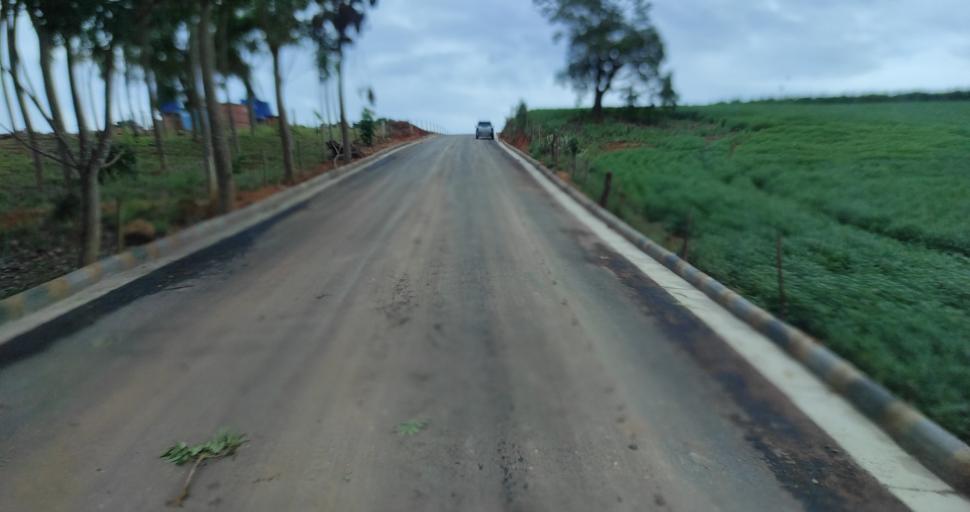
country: BR
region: Minas Gerais
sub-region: Piui
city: Piui
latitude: -20.2763
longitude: -46.3604
